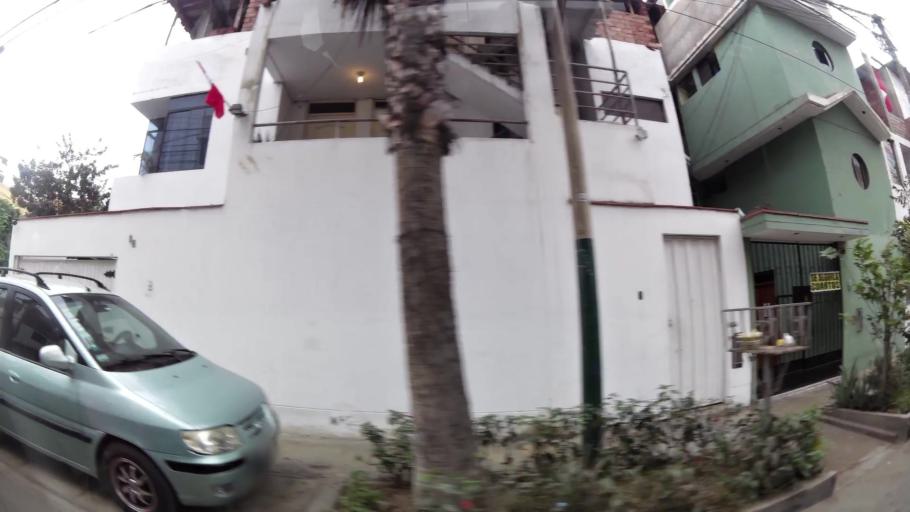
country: PE
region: Lima
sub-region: Lima
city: Surco
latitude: -12.1468
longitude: -76.9975
